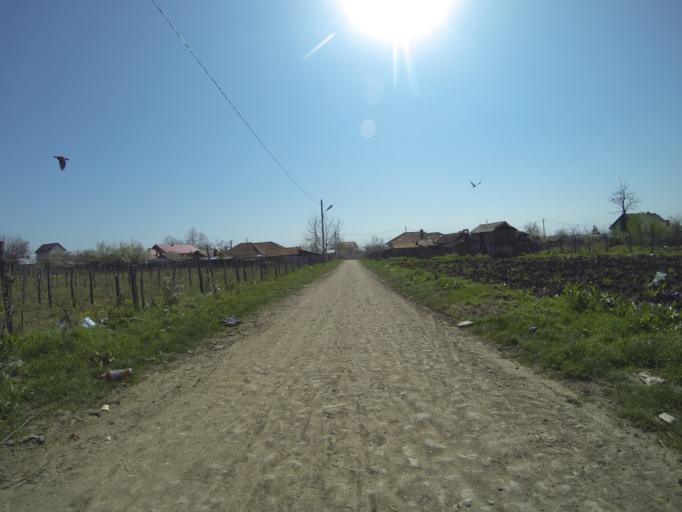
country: RO
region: Dolj
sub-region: Comuna Segarcea
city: Segarcea
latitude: 44.1020
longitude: 23.7348
